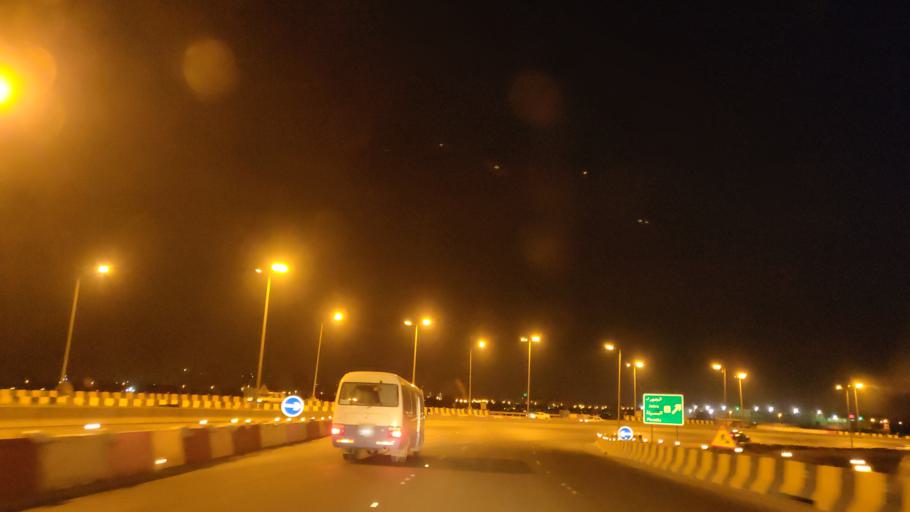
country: KW
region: Al Farwaniyah
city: Al Farwaniyah
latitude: 29.2599
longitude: 47.9548
